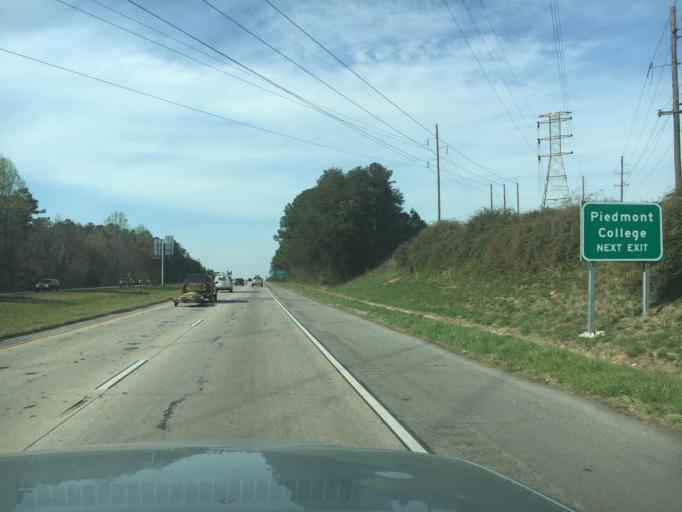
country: US
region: Georgia
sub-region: Habersham County
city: Cornelia
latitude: 34.5281
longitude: -83.5407
